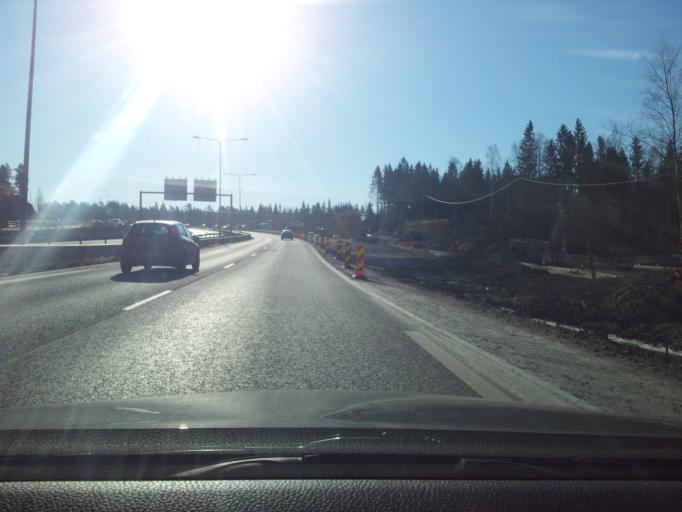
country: FI
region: Uusimaa
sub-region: Helsinki
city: Vantaa
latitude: 60.2327
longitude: 25.0495
